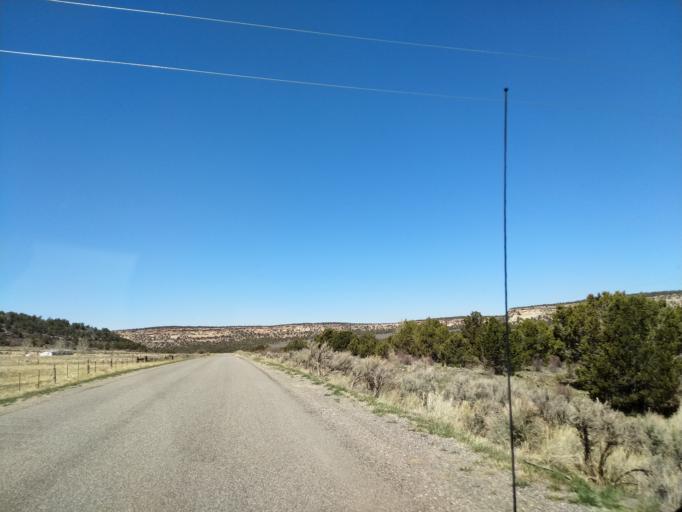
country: US
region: Colorado
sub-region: Mesa County
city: Loma
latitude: 38.9573
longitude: -109.0019
